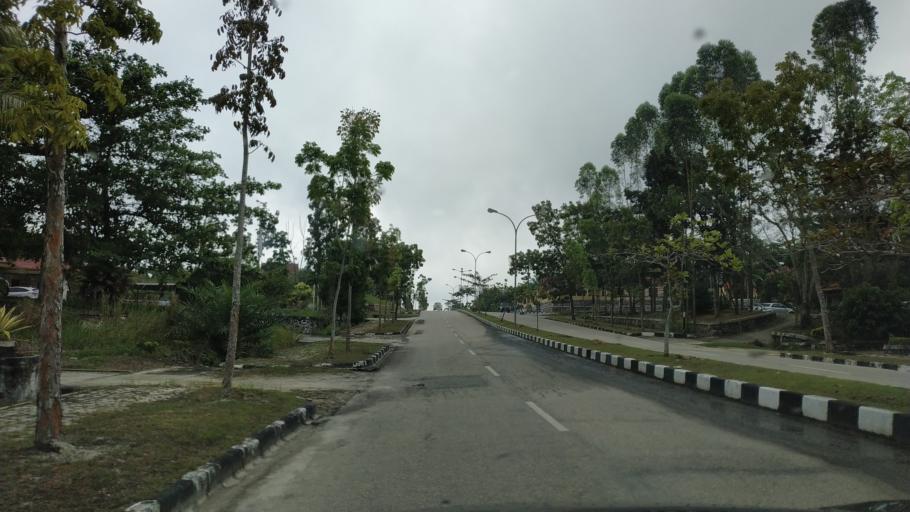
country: ID
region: Riau
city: Pangkalanbunut
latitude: 0.3807
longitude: 101.8256
